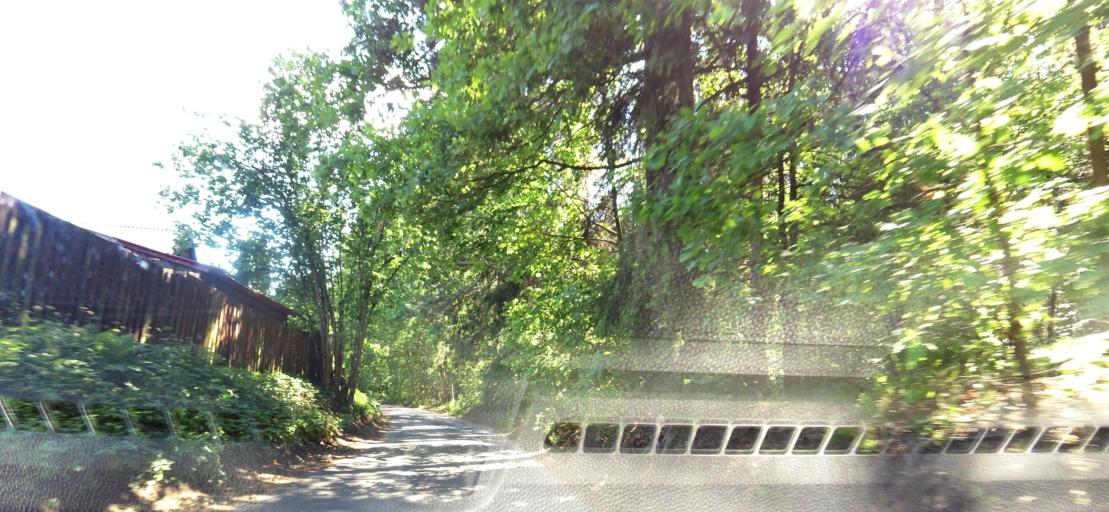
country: LT
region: Vilnius County
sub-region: Vilnius
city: Fabijoniskes
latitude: 54.8252
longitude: 25.3196
